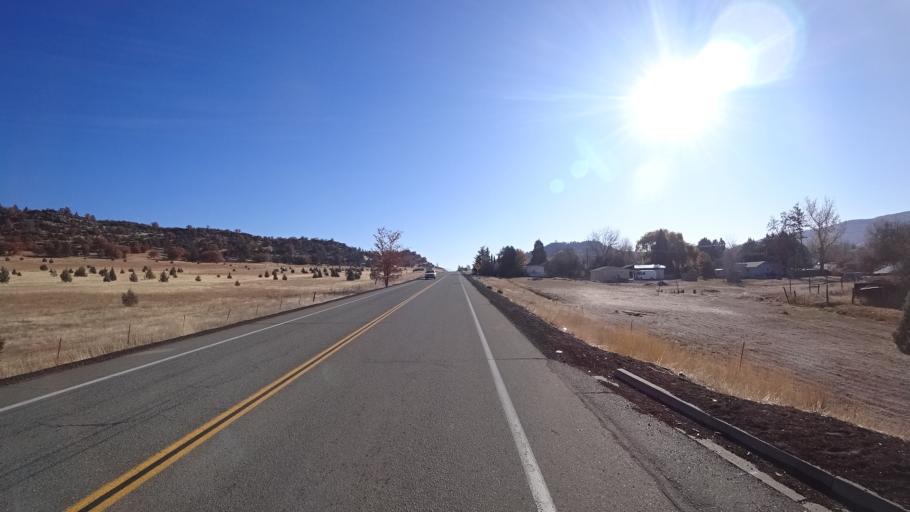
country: US
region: California
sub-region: Siskiyou County
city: Yreka
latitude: 41.7136
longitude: -122.6230
